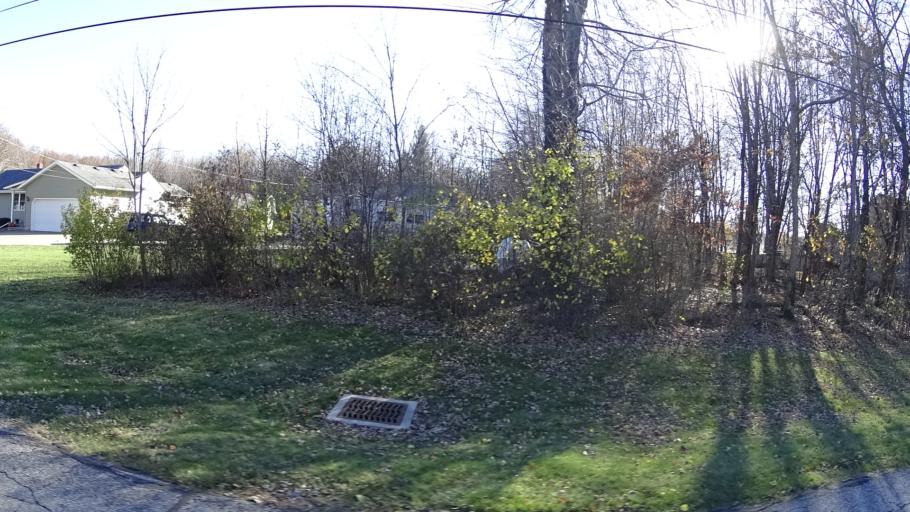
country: US
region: Ohio
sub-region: Lorain County
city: Avon Center
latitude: 41.4476
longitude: -81.9880
